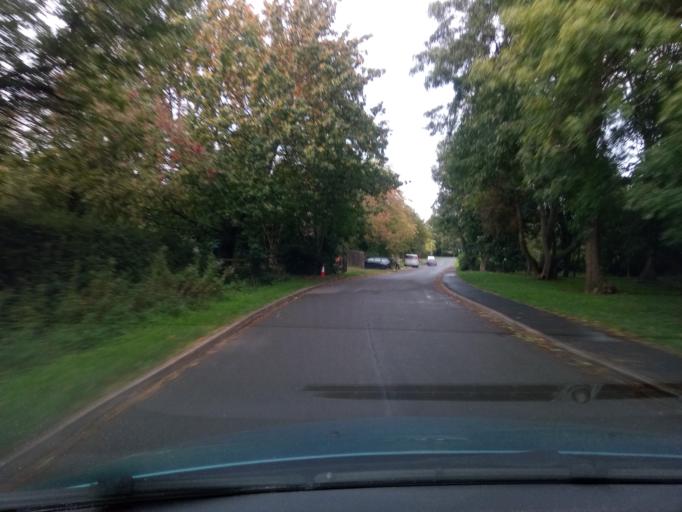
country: GB
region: England
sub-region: Leicestershire
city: Sileby
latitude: 52.7534
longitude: -1.0880
